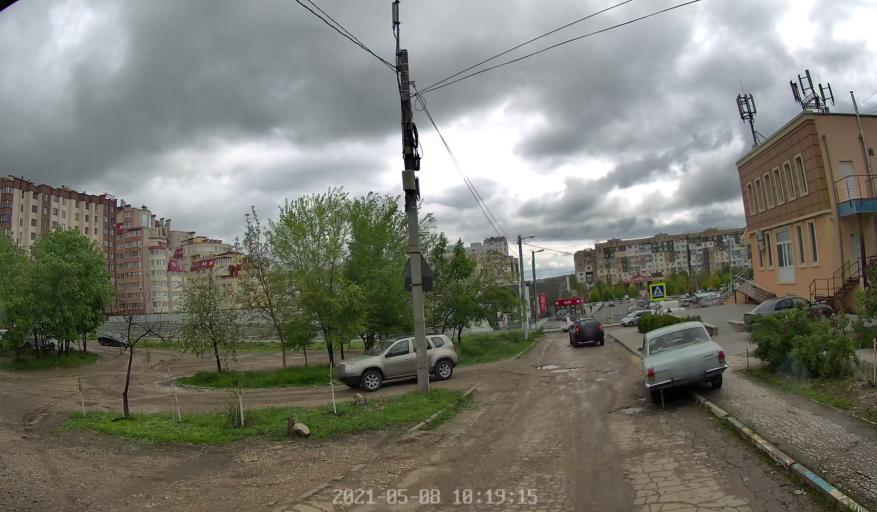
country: MD
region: Chisinau
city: Stauceni
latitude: 47.0535
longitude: 28.8880
